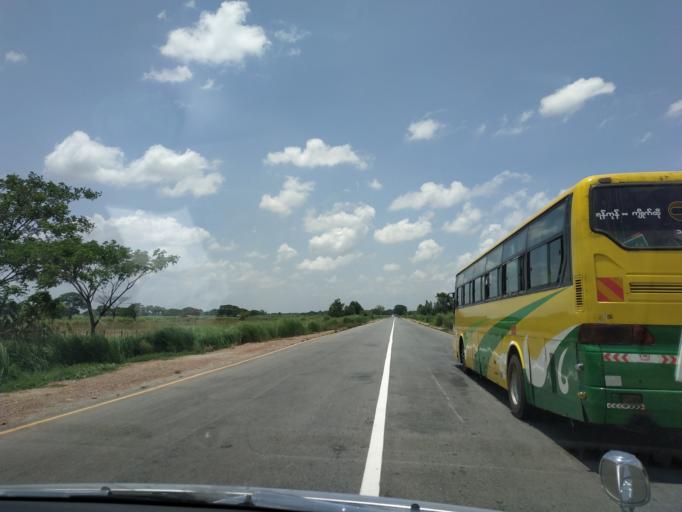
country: MM
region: Bago
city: Thanatpin
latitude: 17.4590
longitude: 96.6477
